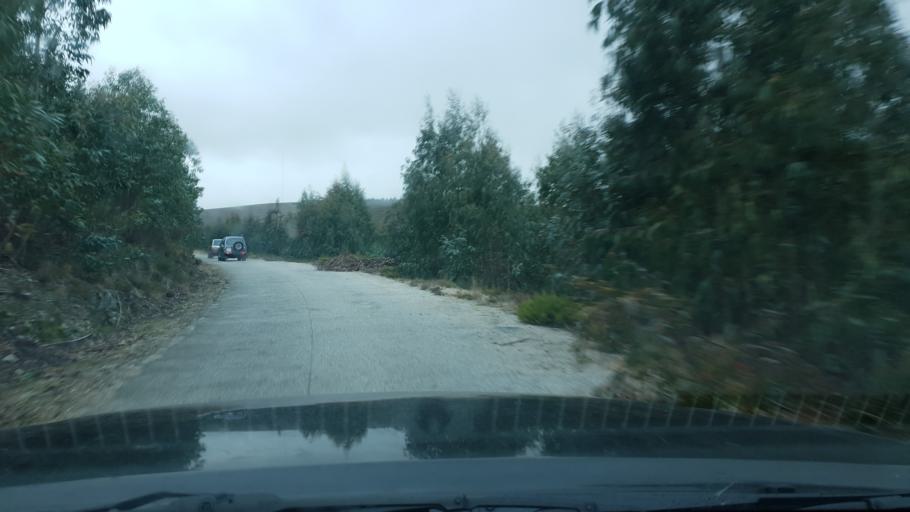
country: PT
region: Viseu
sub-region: Sao Pedro do Sul
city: Sao Pedro do Sul
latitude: 40.8666
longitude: -8.0895
